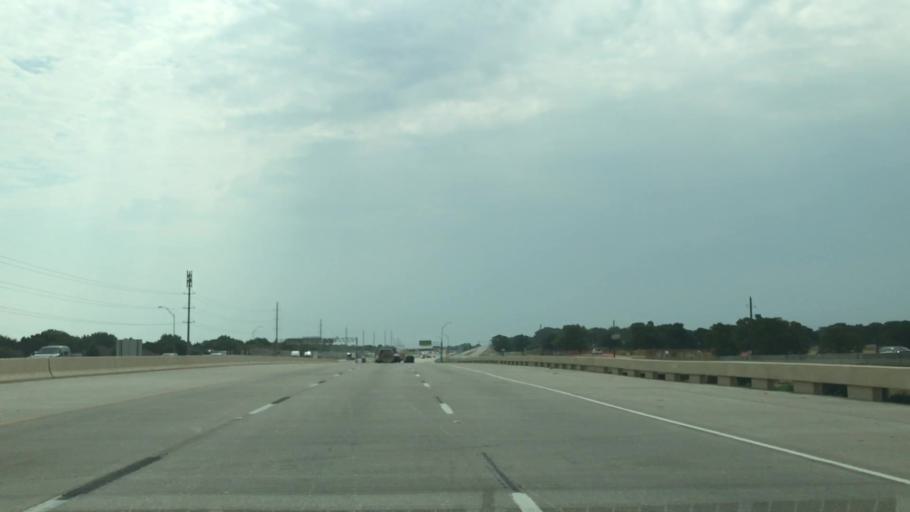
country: US
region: Texas
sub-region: Denton County
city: Roanoke
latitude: 32.9967
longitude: -97.2054
